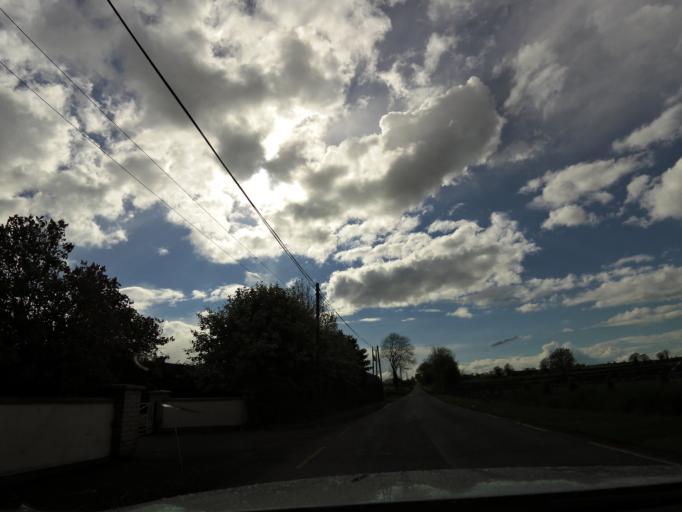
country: IE
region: Leinster
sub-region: Laois
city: Rathdowney
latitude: 52.7522
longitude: -7.6157
